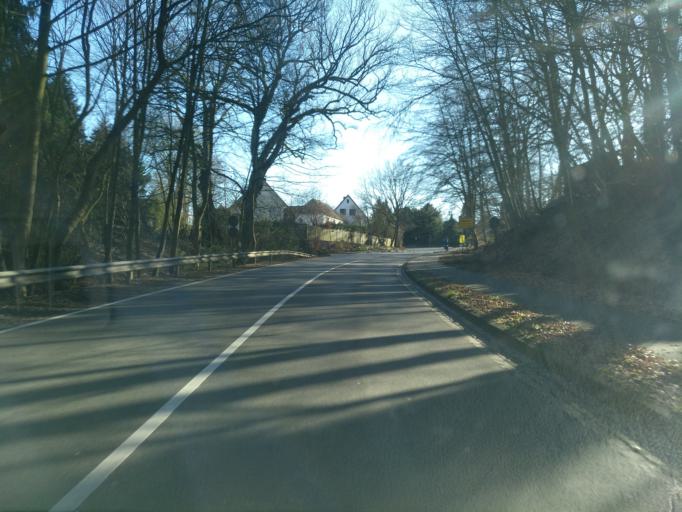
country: DE
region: Lower Saxony
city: Seevetal
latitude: 53.4447
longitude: 9.9025
